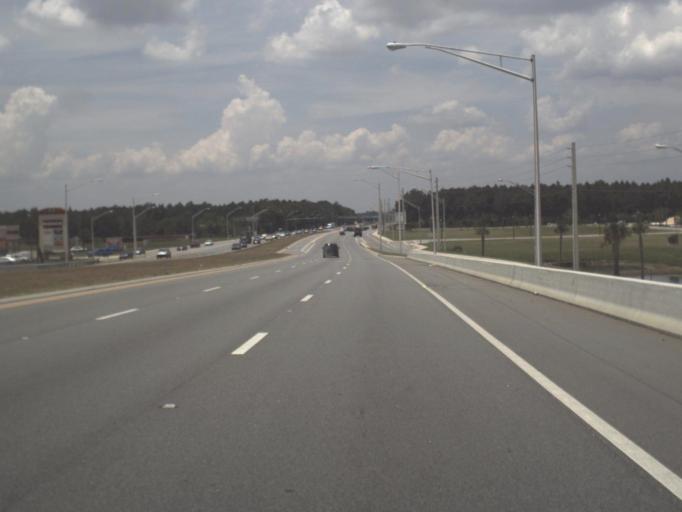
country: US
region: Florida
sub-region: Duval County
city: Atlantic Beach
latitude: 30.3203
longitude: -81.4919
